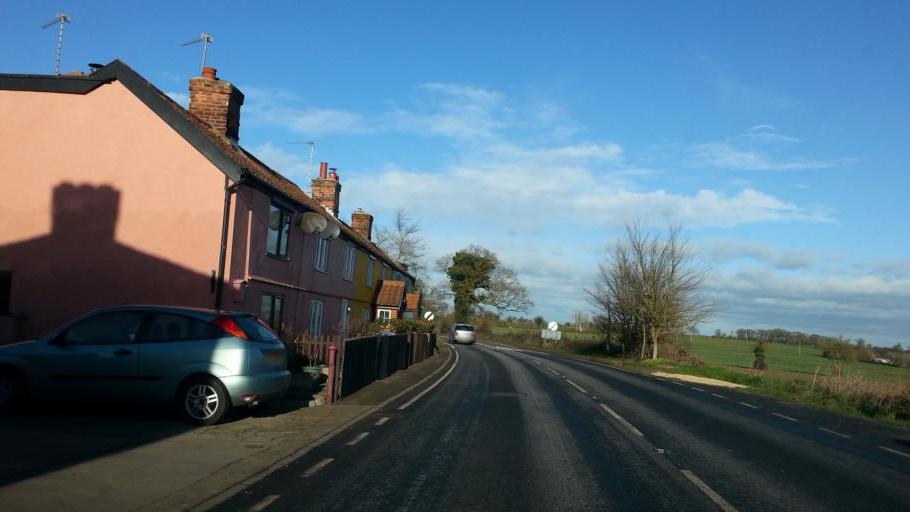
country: GB
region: England
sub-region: Suffolk
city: Halesworth
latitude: 52.3170
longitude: 1.5199
